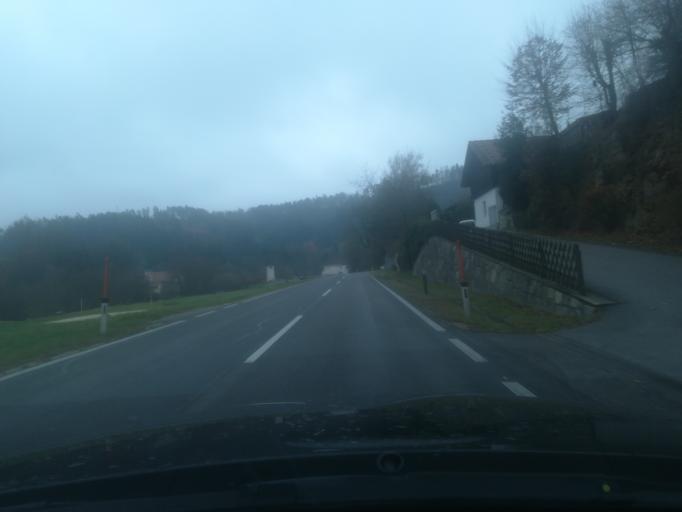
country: AT
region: Upper Austria
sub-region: Politischer Bezirk Perg
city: Perg
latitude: 48.3238
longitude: 14.5657
